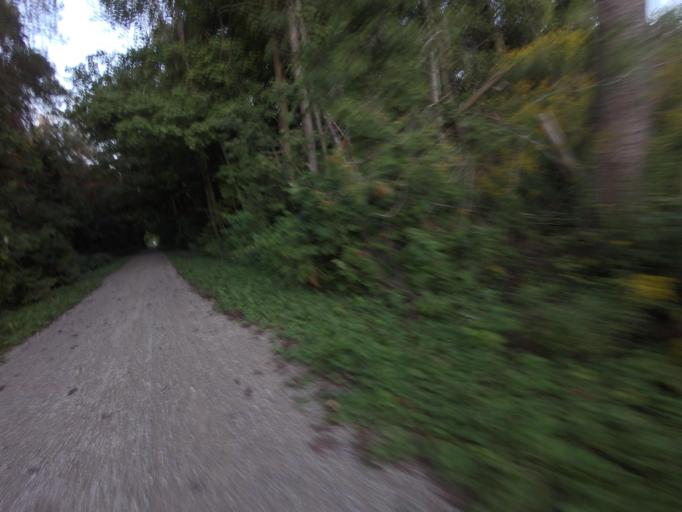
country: CA
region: Ontario
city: Goderich
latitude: 43.7519
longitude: -81.6217
